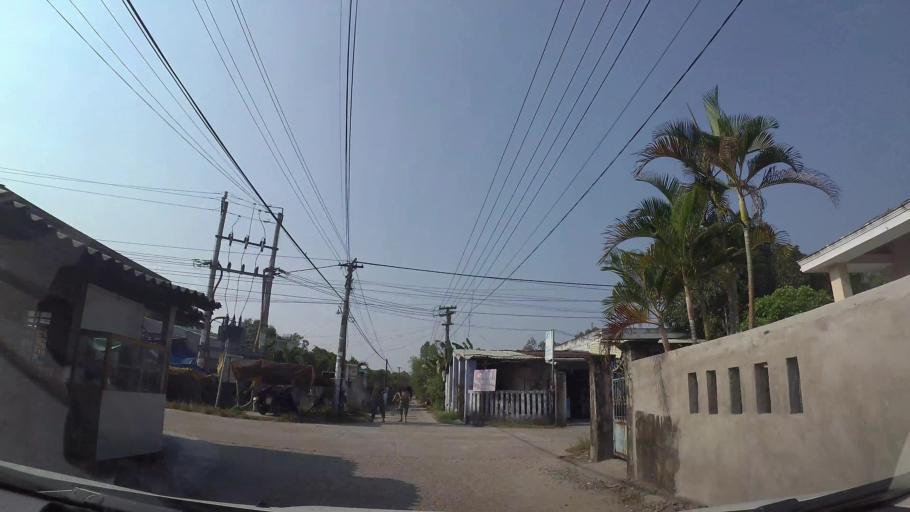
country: VN
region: Da Nang
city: Ngu Hanh Son
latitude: 15.9569
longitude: 108.2647
